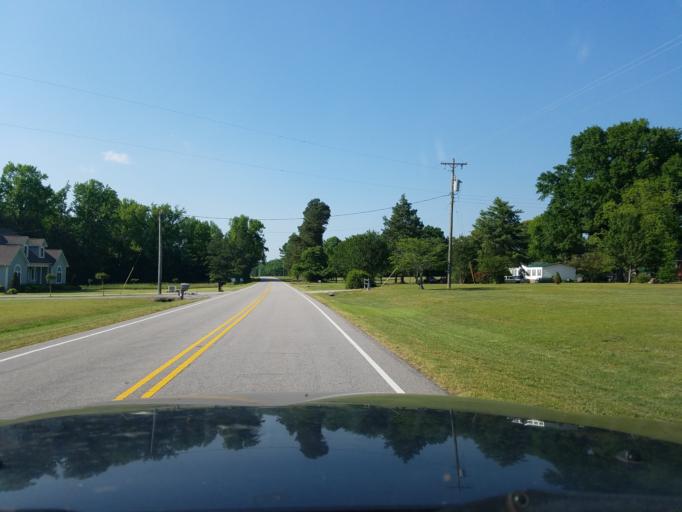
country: US
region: North Carolina
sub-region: Vance County
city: Henderson
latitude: 36.3988
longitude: -78.3683
